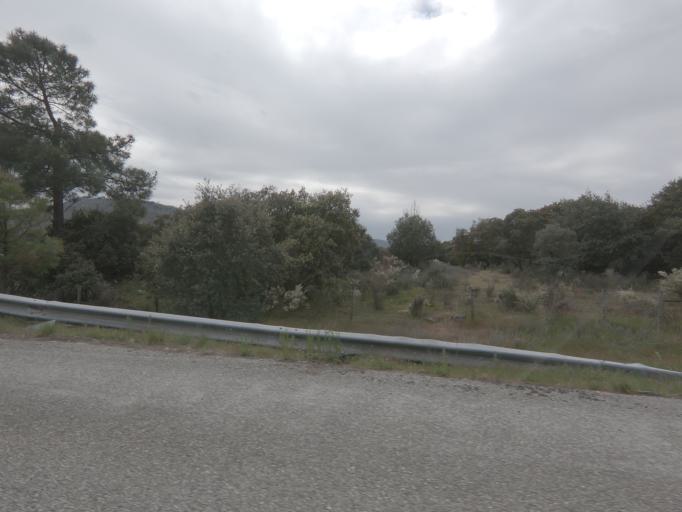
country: PT
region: Guarda
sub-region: Celorico da Beira
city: Celorico da Beira
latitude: 40.6256
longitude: -7.3070
